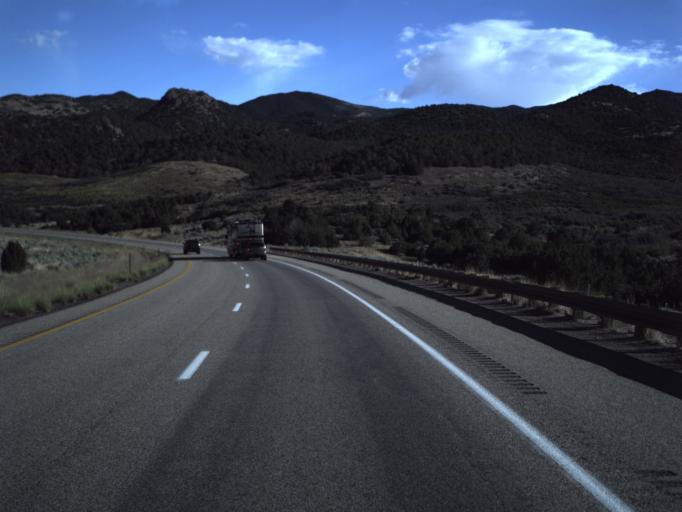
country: US
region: Utah
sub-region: Beaver County
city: Beaver
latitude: 38.6031
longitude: -112.5062
